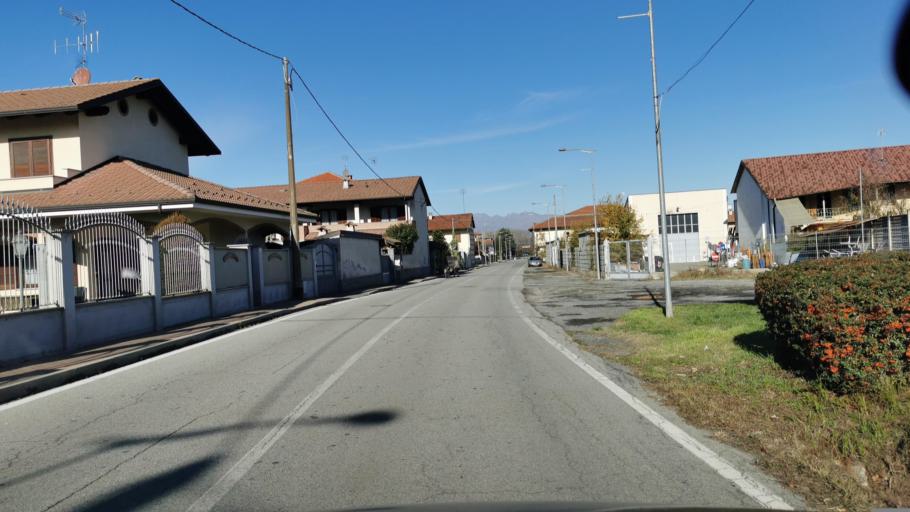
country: IT
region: Piedmont
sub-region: Provincia di Torino
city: Volpiano
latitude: 45.2067
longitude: 7.7744
